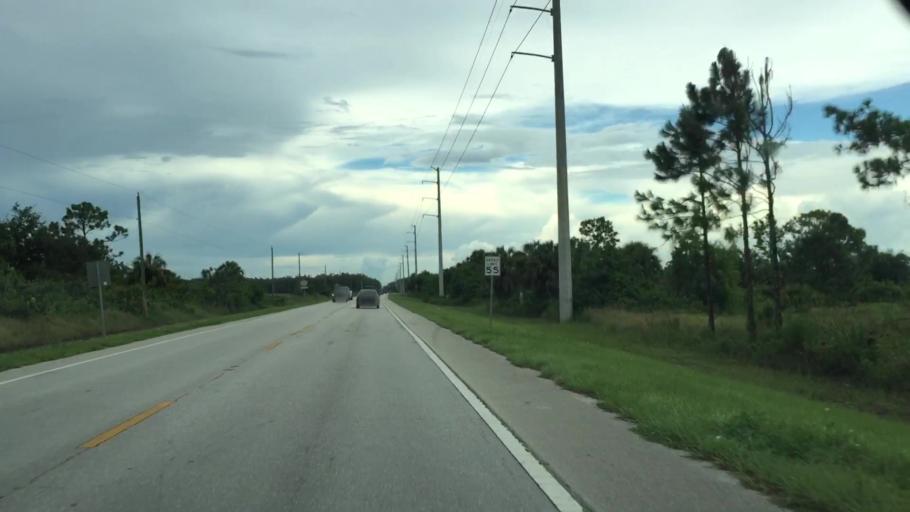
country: US
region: Florida
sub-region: Collier County
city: Orangetree
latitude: 26.3207
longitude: -81.5950
